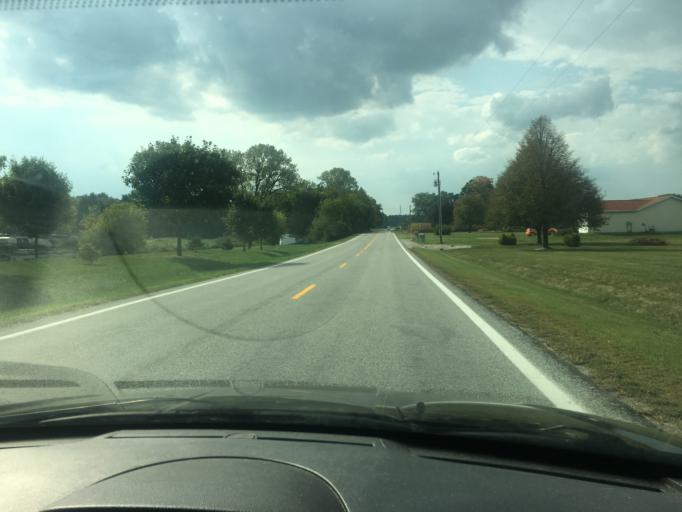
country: US
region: Ohio
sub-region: Champaign County
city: Urbana
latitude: 40.1567
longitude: -83.7709
